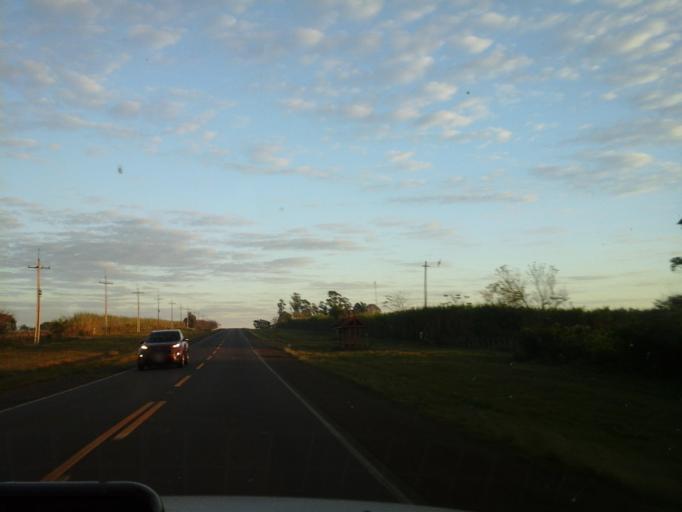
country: PY
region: Misiones
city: San Patricio
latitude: -27.0206
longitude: -56.7131
